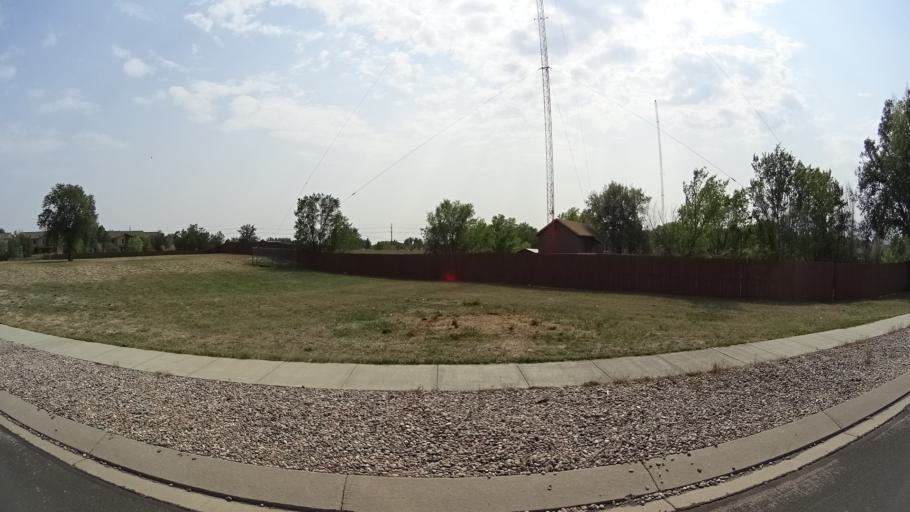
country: US
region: Colorado
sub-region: El Paso County
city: Cimarron Hills
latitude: 38.8269
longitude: -104.7416
